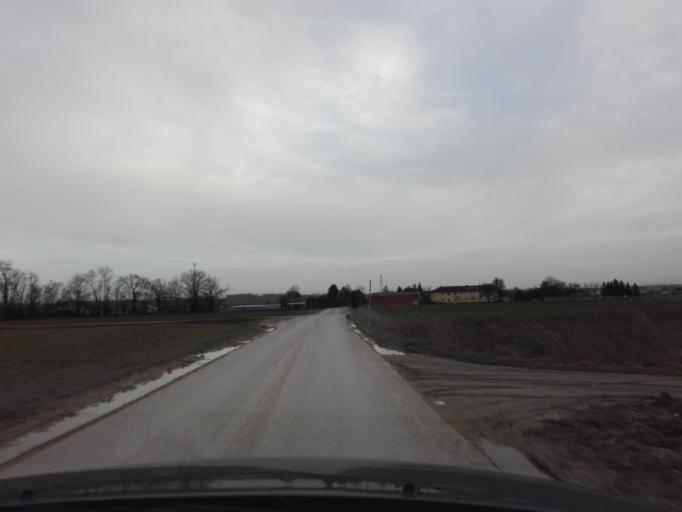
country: AT
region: Upper Austria
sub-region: Politischer Bezirk Linz-Land
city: Horsching
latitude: 48.2101
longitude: 14.1549
